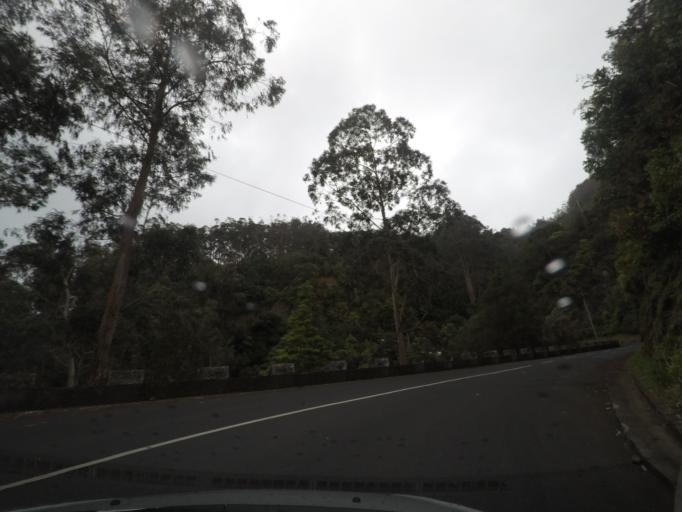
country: PT
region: Madeira
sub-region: Santa Cruz
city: Camacha
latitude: 32.7486
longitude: -16.8314
